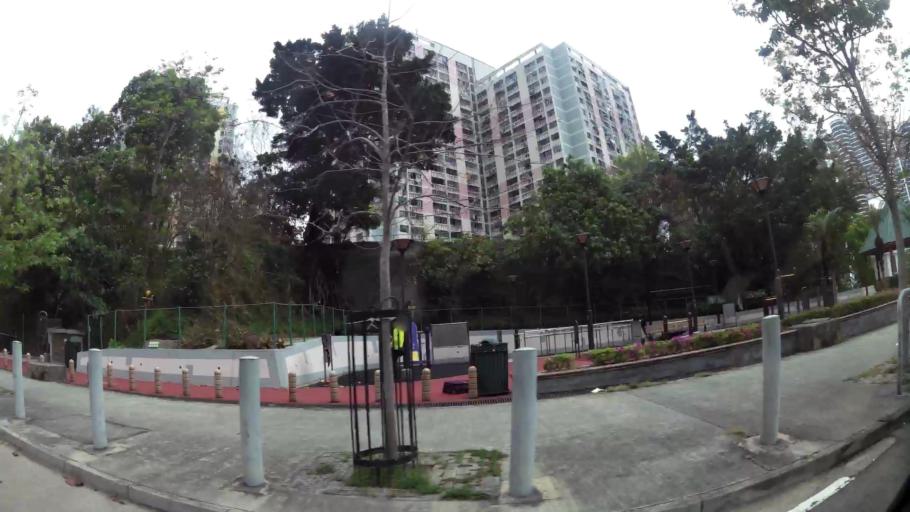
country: HK
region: Central and Western
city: Central
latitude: 22.2544
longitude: 114.1368
